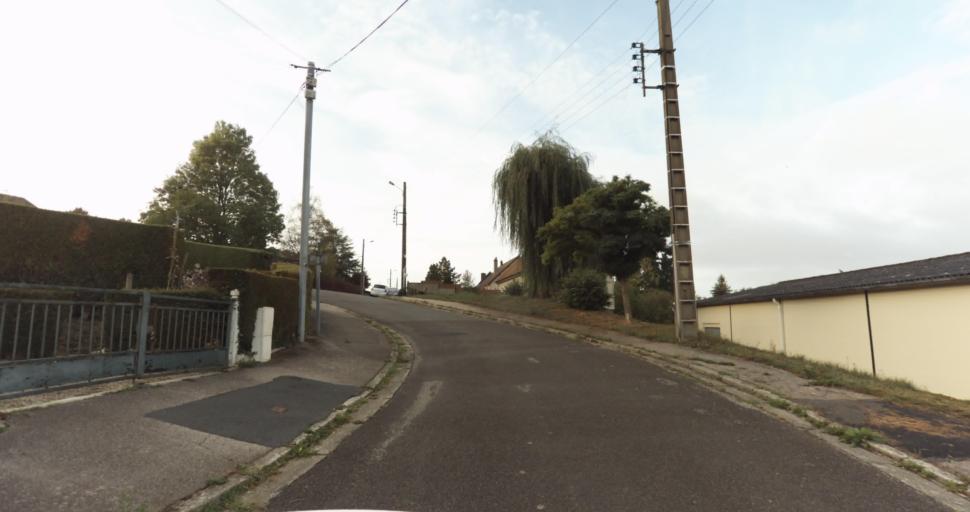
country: FR
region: Lower Normandy
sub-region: Departement de l'Orne
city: Vimoutiers
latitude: 48.9286
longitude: 0.2034
